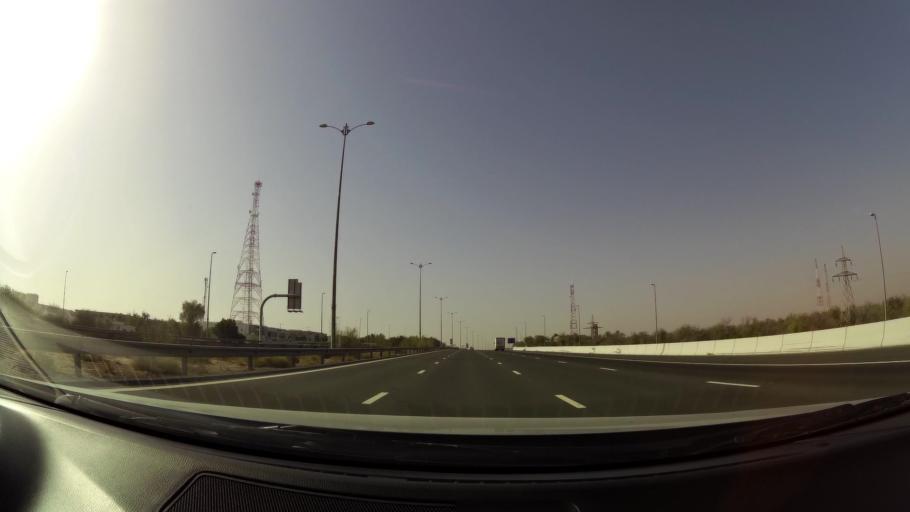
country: OM
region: Al Buraimi
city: Al Buraymi
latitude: 24.5806
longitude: 55.7432
